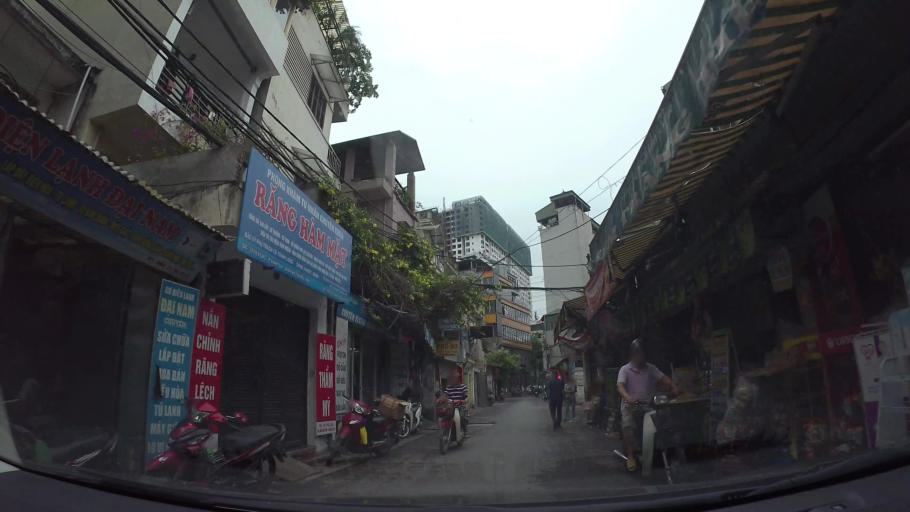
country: VN
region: Ha Noi
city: Hai BaTrung
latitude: 20.9996
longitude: 105.8628
